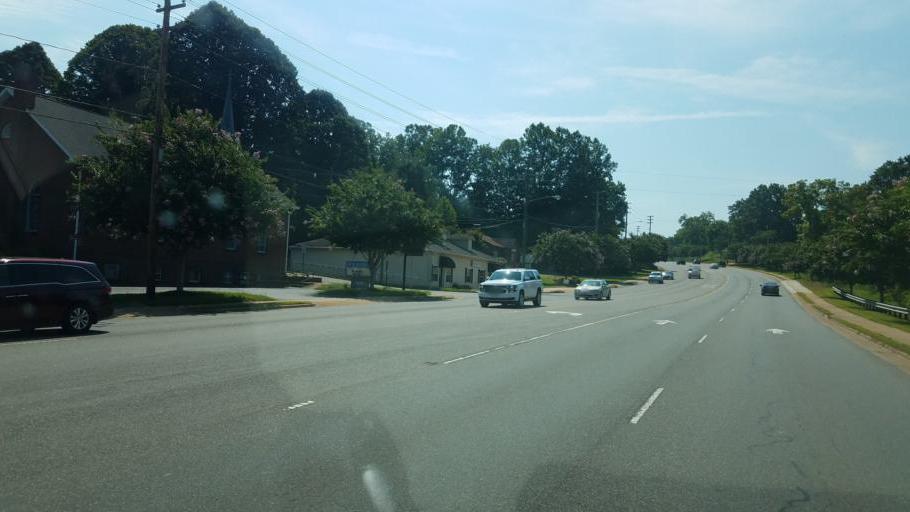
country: US
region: North Carolina
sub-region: Burke County
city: Morganton
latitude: 35.7373
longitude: -81.6777
